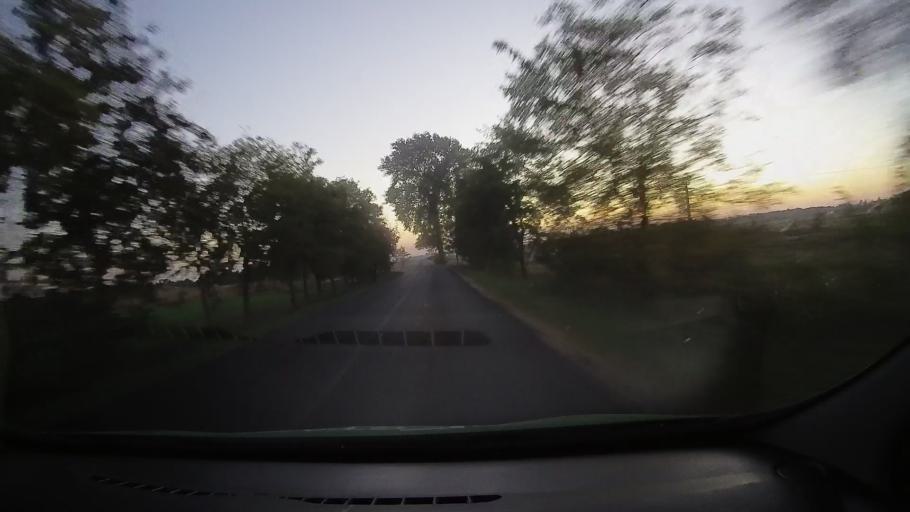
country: RO
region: Bihor
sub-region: Comuna Simian
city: Simian
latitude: 47.5082
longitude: 22.0963
